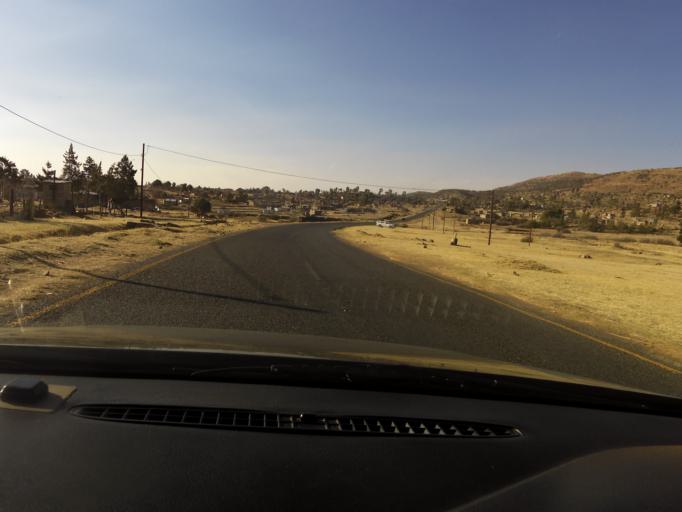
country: LS
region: Mafeteng
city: Mafeteng
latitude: -29.8469
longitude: 27.2291
